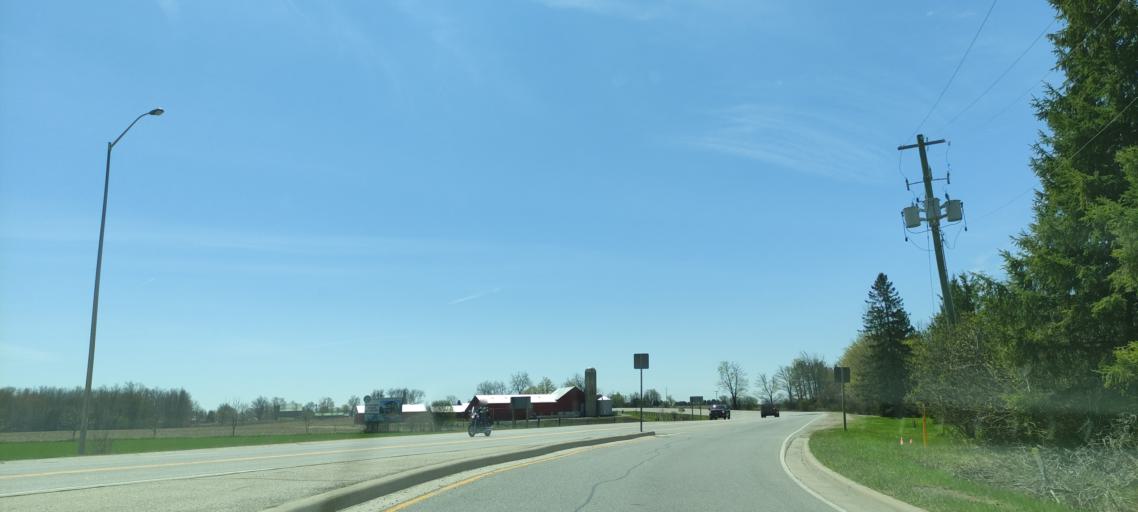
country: CA
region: Ontario
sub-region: Wellington County
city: Guelph
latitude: 43.5928
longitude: -80.3068
